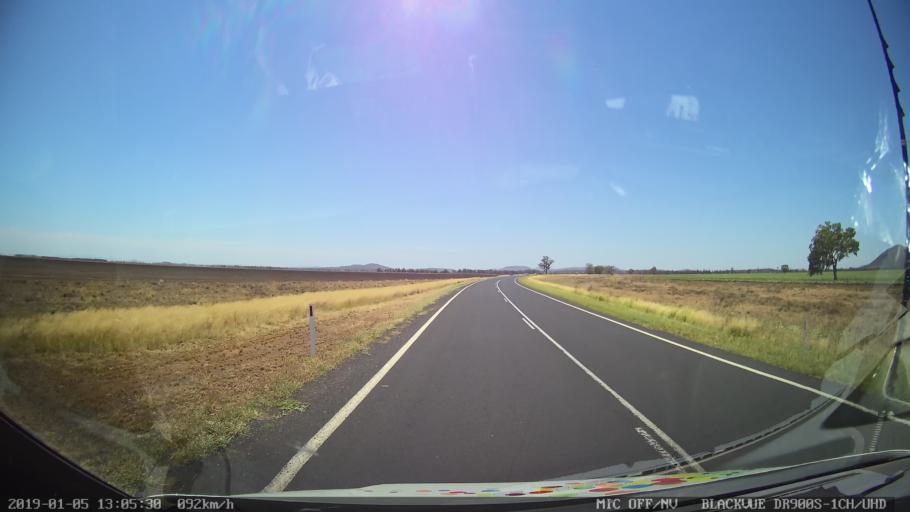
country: AU
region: New South Wales
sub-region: Gunnedah
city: Gunnedah
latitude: -31.0949
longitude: 149.8542
